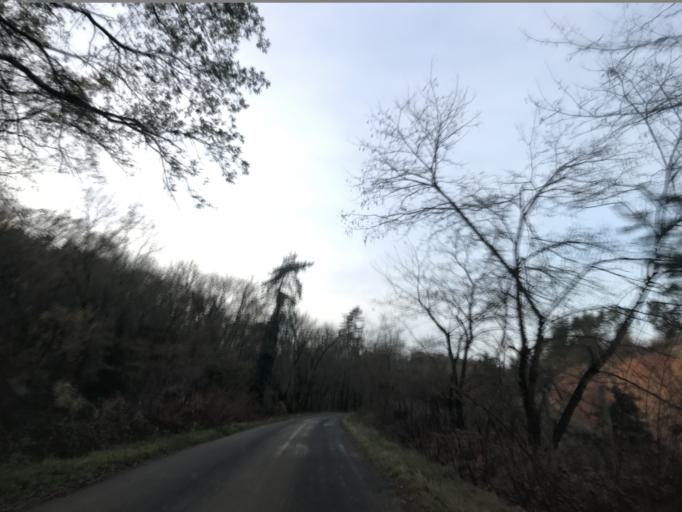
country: FR
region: Auvergne
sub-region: Departement du Puy-de-Dome
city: Courpiere
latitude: 45.7624
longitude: 3.5136
